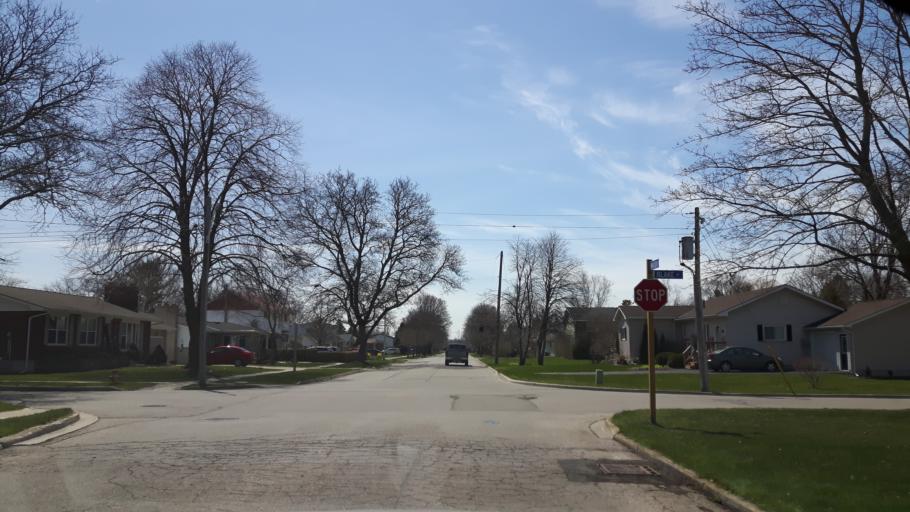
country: CA
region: Ontario
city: Goderich
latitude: 43.7356
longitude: -81.7216
